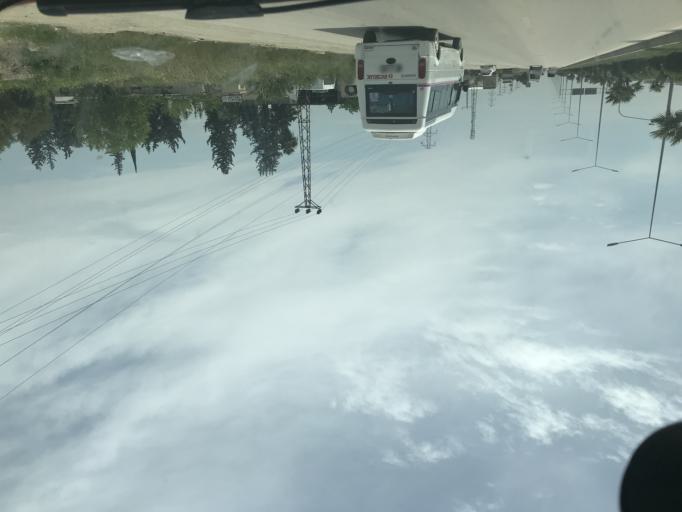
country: TR
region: Adana
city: Yuregir
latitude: 36.9823
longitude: 35.4281
